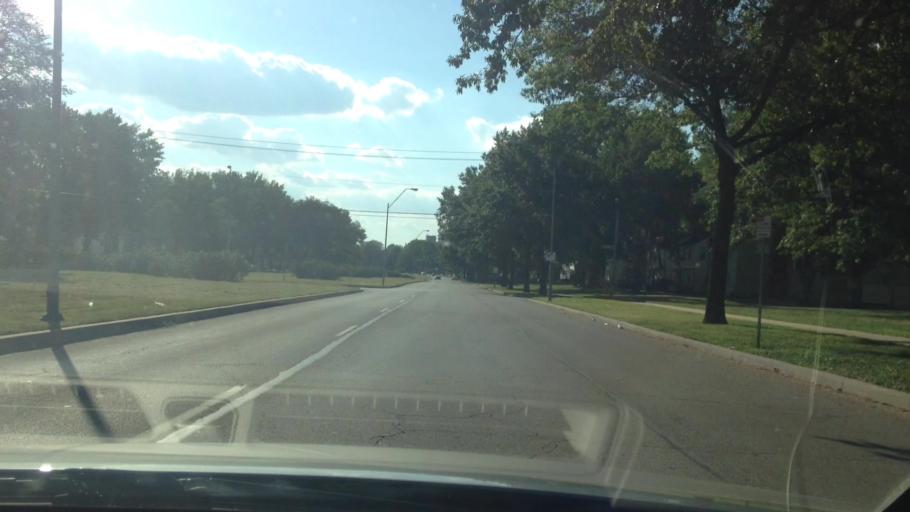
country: US
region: Kansas
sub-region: Johnson County
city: Mission Hills
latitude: 39.0078
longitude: -94.5462
